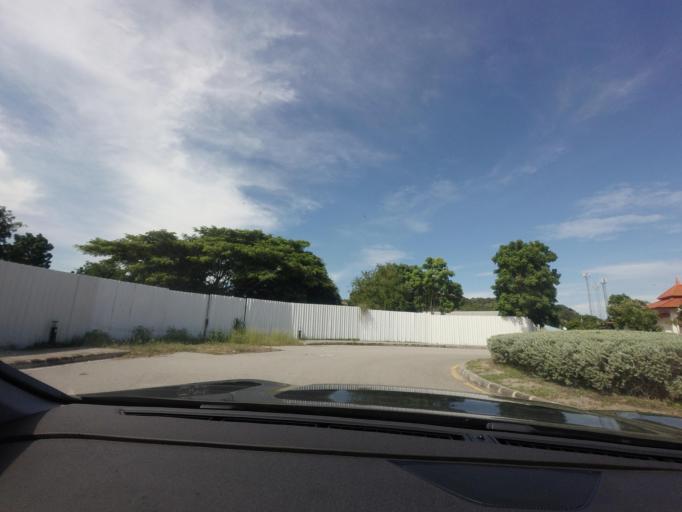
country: TH
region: Prachuap Khiri Khan
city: Hua Hin
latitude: 12.5165
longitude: 99.9617
